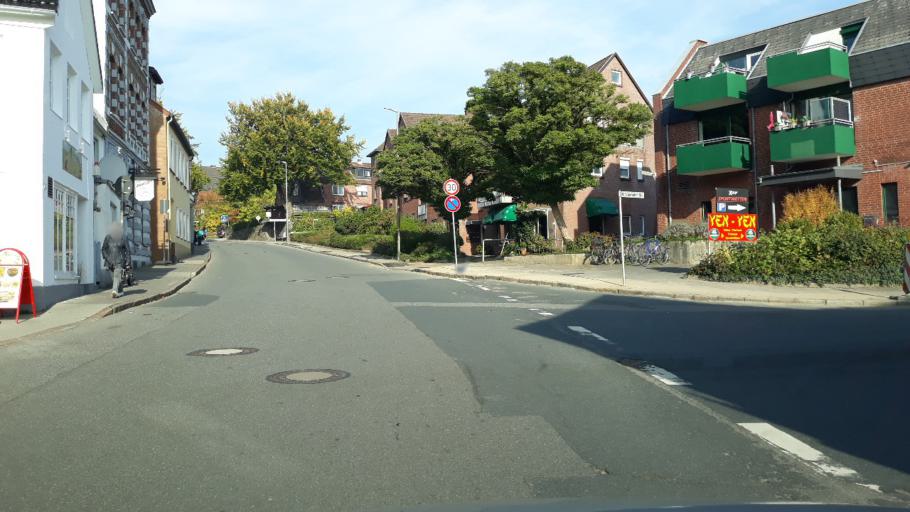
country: DE
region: Schleswig-Holstein
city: Schleswig
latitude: 54.5180
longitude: 9.5702
